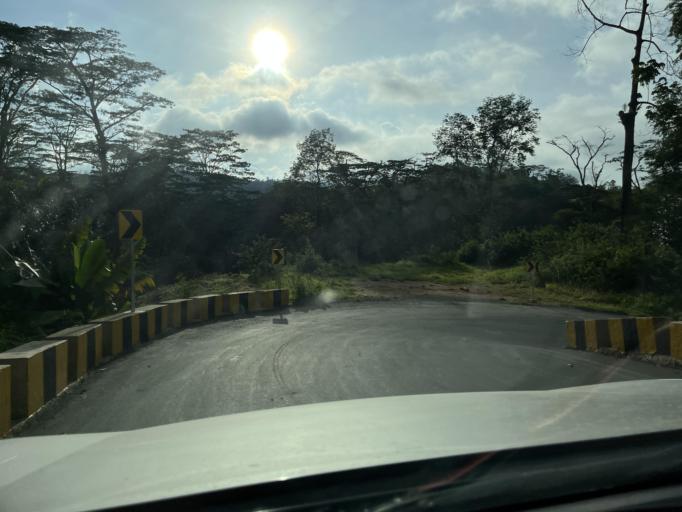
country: TL
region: Dili
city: Dili
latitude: -8.6031
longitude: 125.6050
